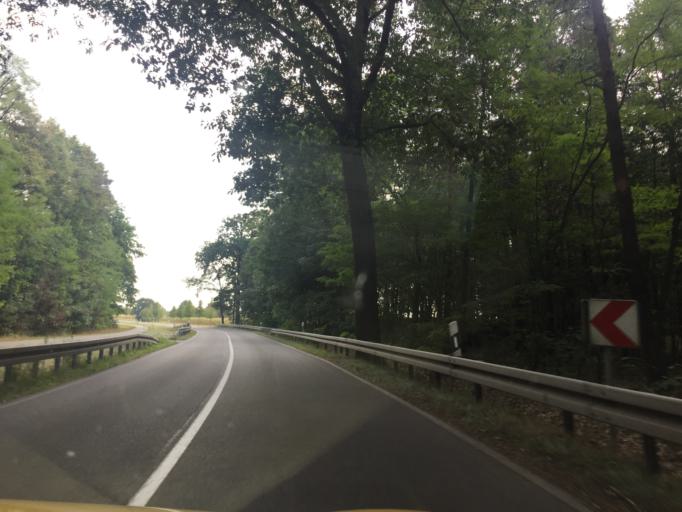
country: DE
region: Brandenburg
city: Welzow
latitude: 51.5601
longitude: 14.1805
